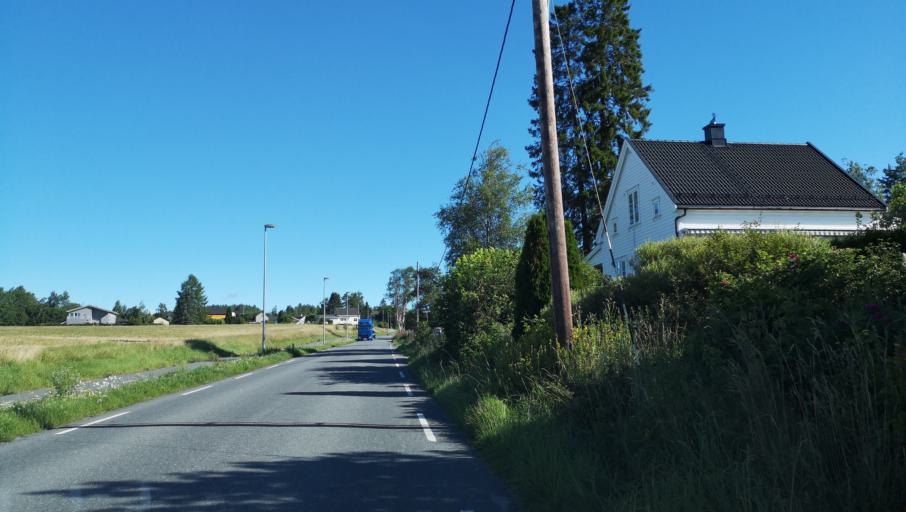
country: NO
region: Ostfold
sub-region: Hobol
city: Knappstad
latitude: 59.6212
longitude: 11.0236
